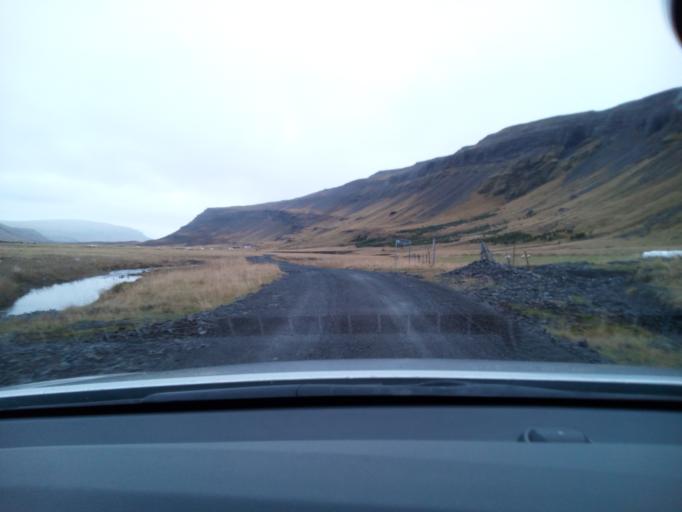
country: IS
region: South
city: Hveragerdi
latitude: 64.3634
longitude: -21.3111
